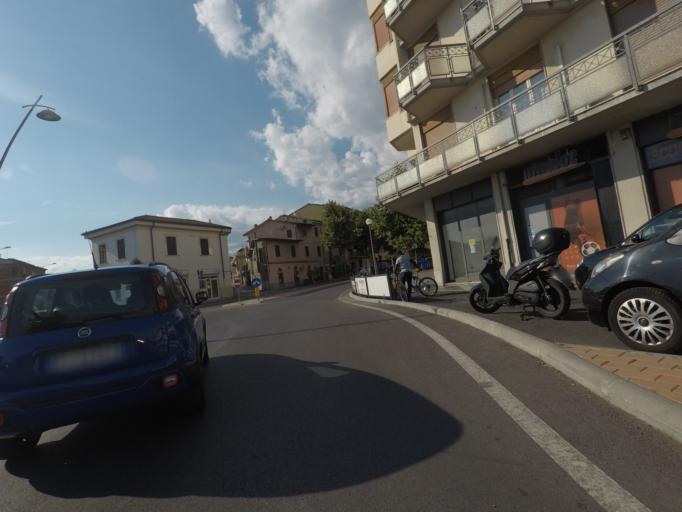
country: IT
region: Tuscany
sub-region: Provincia di Massa-Carrara
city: Massa
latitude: 44.0247
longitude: 10.1366
